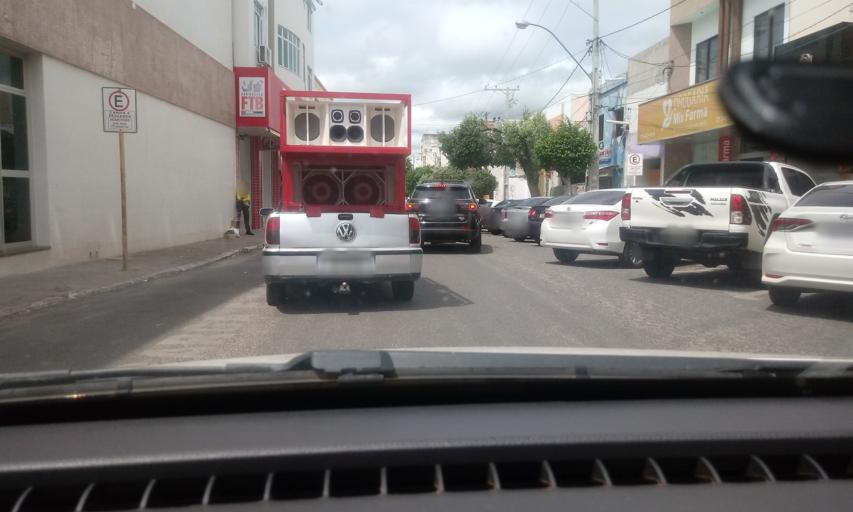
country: BR
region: Bahia
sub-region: Guanambi
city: Guanambi
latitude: -14.2260
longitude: -42.7792
